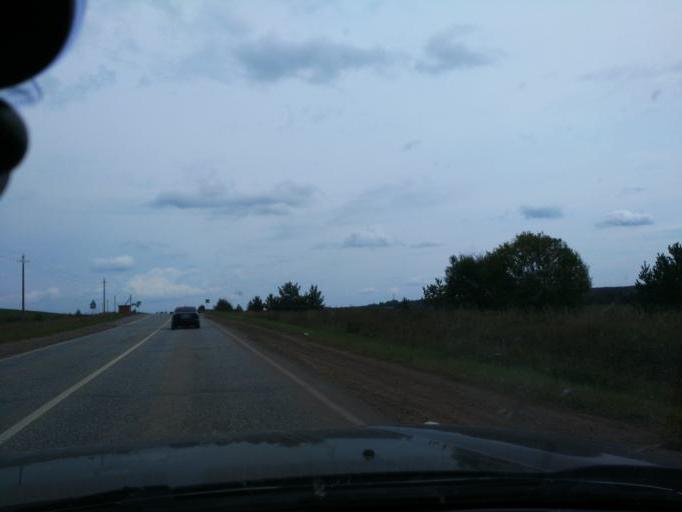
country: RU
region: Perm
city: Kuyeda
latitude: 56.4695
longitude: 55.7340
